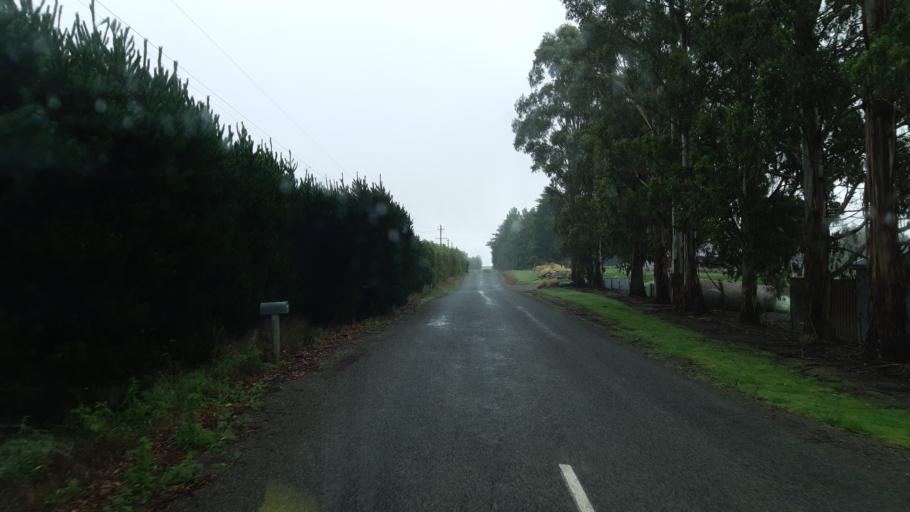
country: NZ
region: Otago
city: Oamaru
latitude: -44.9374
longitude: 170.7205
